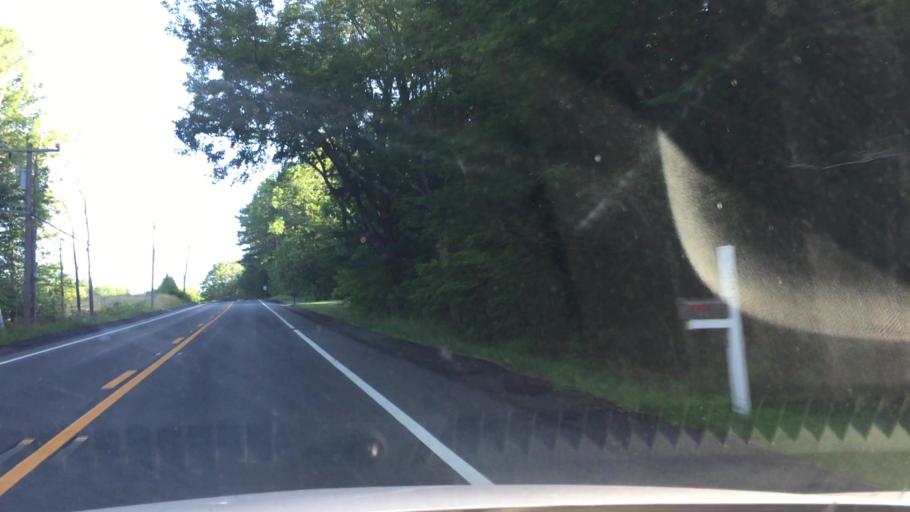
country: US
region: Massachusetts
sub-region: Berkshire County
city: Becket
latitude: 42.2720
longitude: -73.0543
